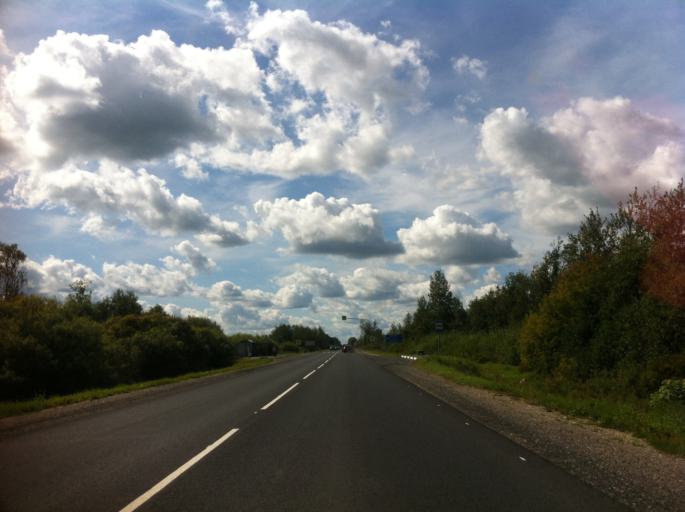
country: RU
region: Pskov
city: Izborsk
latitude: 57.7405
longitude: 28.0109
